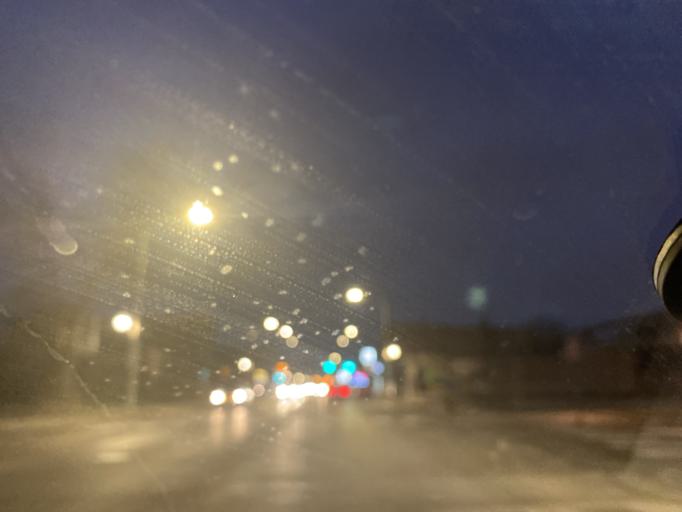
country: US
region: Illinois
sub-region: Cook County
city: Chicago
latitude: 41.7796
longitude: -87.6559
